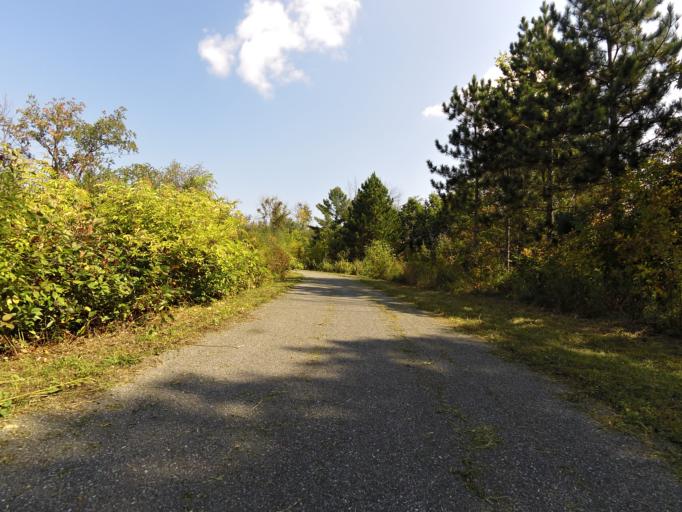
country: CA
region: Ontario
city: Bells Corners
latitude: 45.2630
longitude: -75.7325
